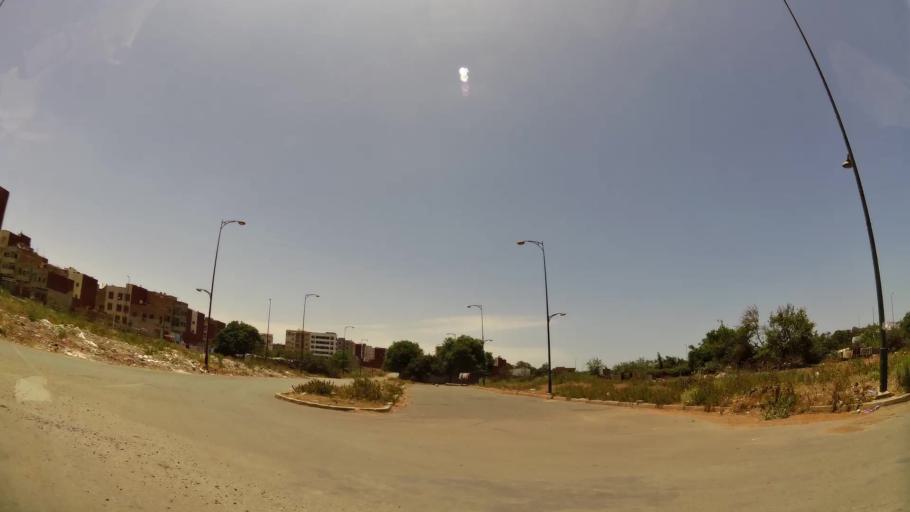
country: MA
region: Gharb-Chrarda-Beni Hssen
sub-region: Kenitra Province
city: Kenitra
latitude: 34.2637
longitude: -6.6249
